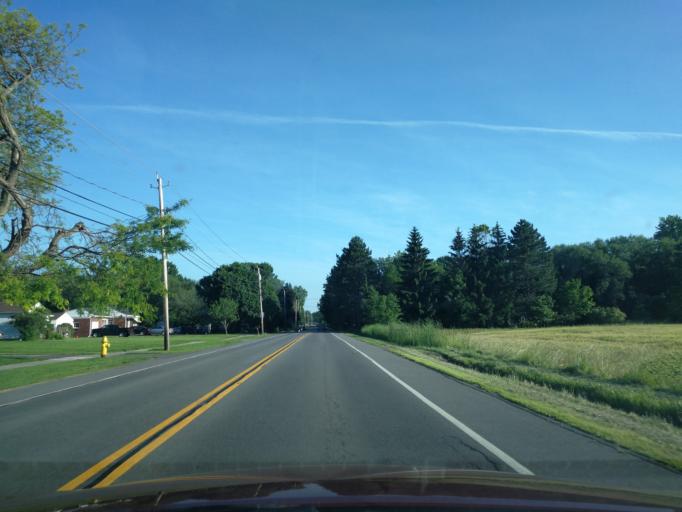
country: US
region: New York
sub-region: Monroe County
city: Greece
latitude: 43.2576
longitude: -77.7155
